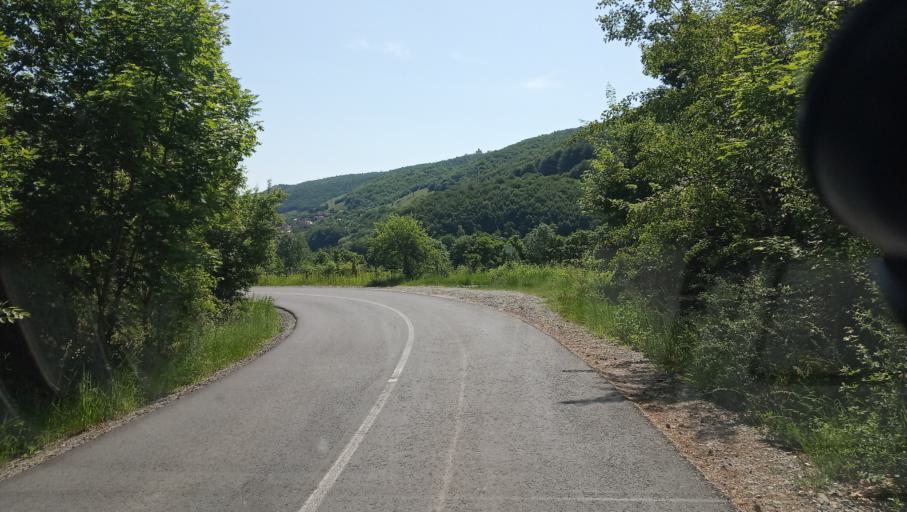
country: RO
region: Cluj
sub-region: Comuna Capusu Mare
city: Capusu Mare
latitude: 46.7328
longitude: 23.3068
